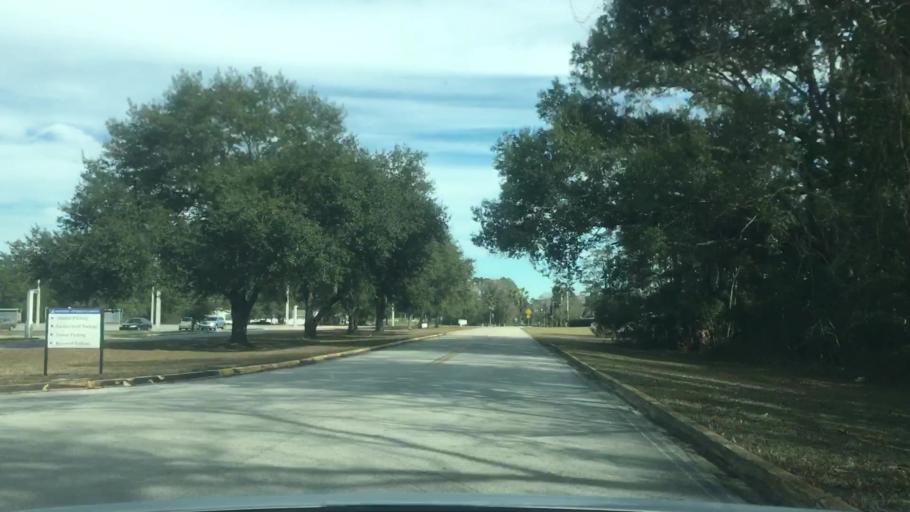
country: US
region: Florida
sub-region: Duval County
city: Neptune Beach
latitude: 30.2908
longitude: -81.5073
